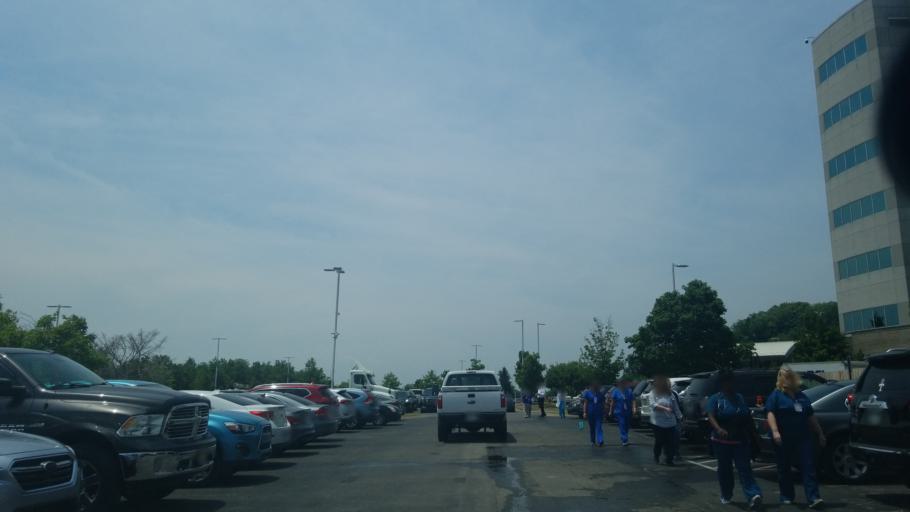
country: US
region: Tennessee
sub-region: Davidson County
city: Goodlettsville
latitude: 36.2449
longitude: -86.7488
